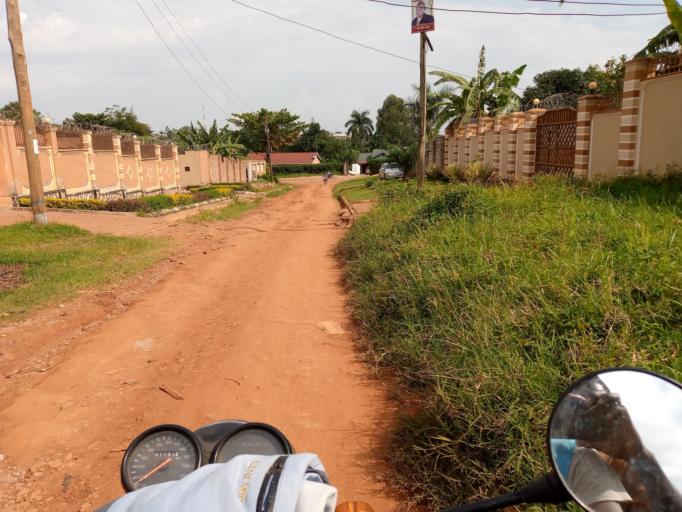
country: UG
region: Eastern Region
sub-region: Mbale District
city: Mbale
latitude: 1.0779
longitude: 34.1704
